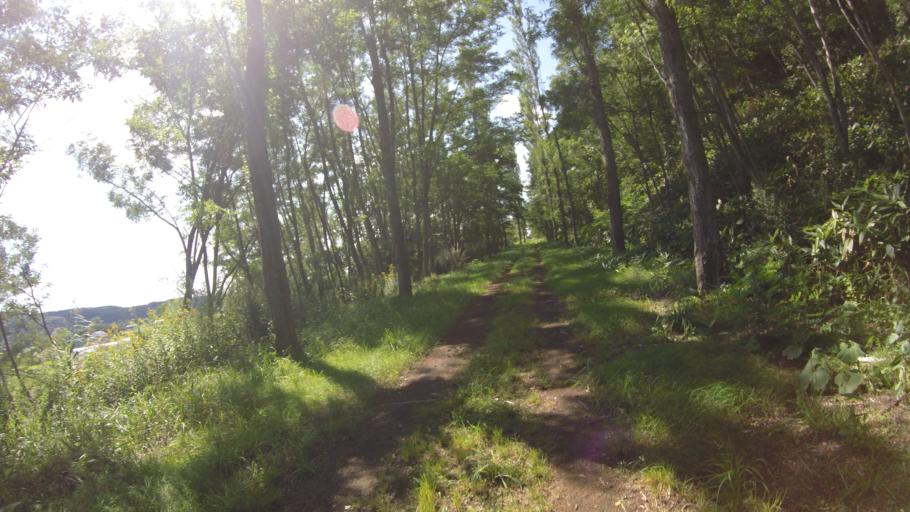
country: JP
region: Hokkaido
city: Iwamizawa
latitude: 43.1599
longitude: 141.8024
